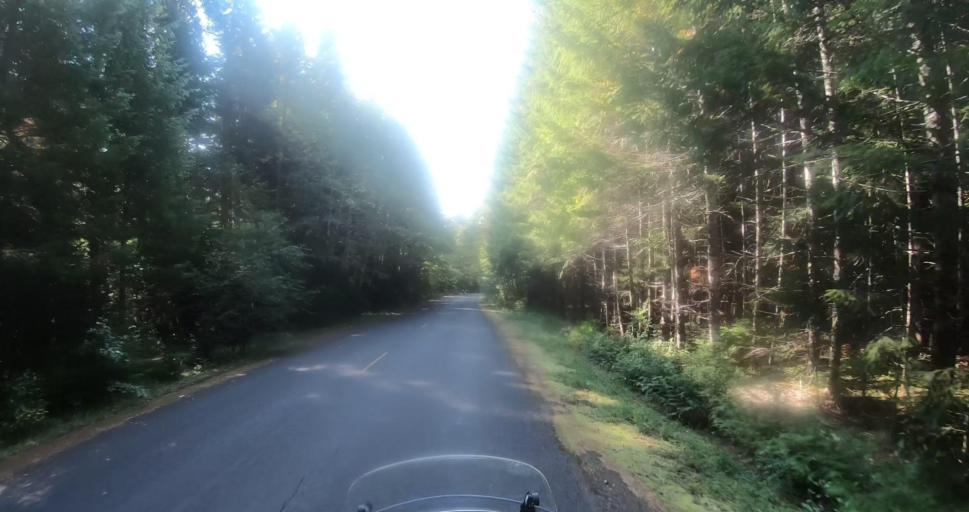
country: US
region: Washington
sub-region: Skamania County
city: Carson
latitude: 46.1840
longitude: -121.8400
